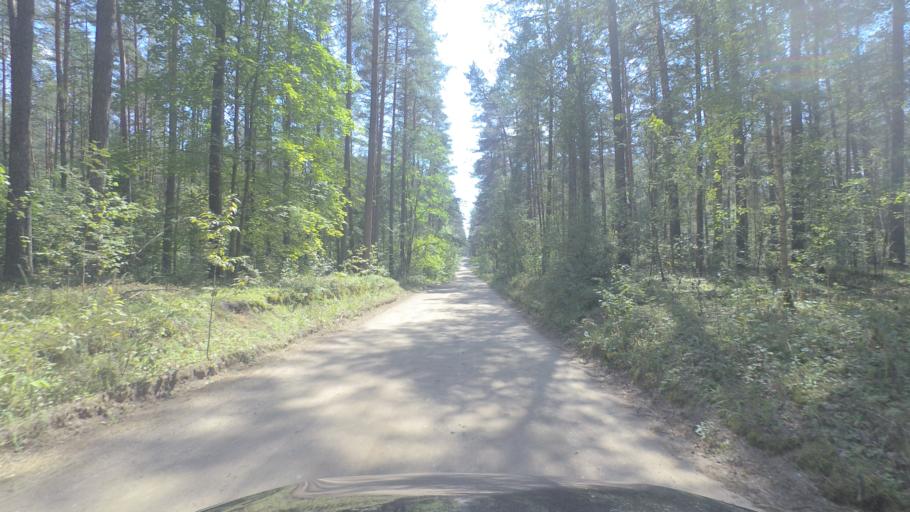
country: LT
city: Nemencine
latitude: 54.8462
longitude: 25.4979
